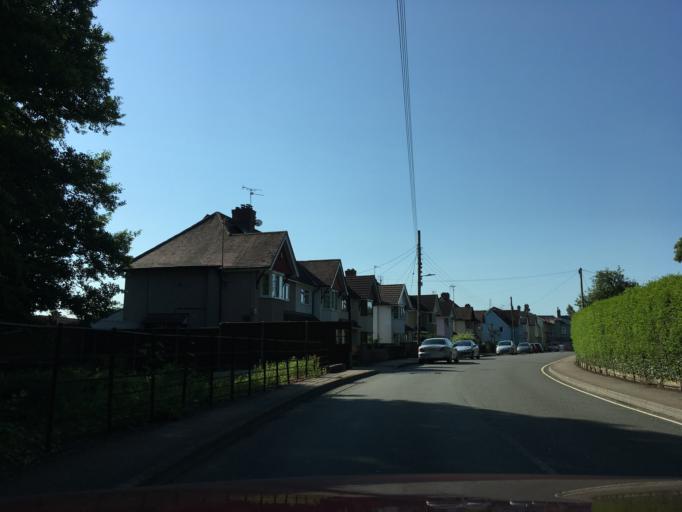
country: GB
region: England
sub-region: Gloucestershire
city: Lydney
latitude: 51.7278
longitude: -2.5318
